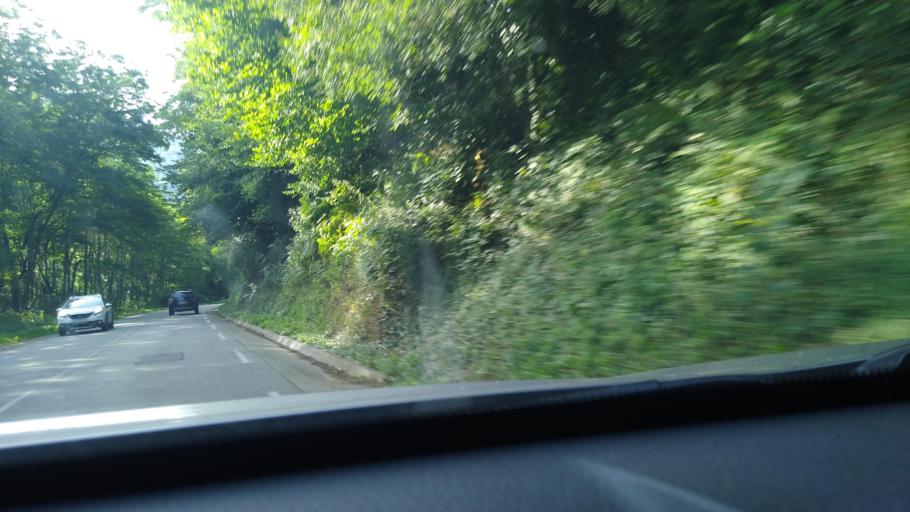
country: FR
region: Midi-Pyrenees
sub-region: Departement de l'Ariege
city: Saint-Girons
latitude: 42.9316
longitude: 1.1788
